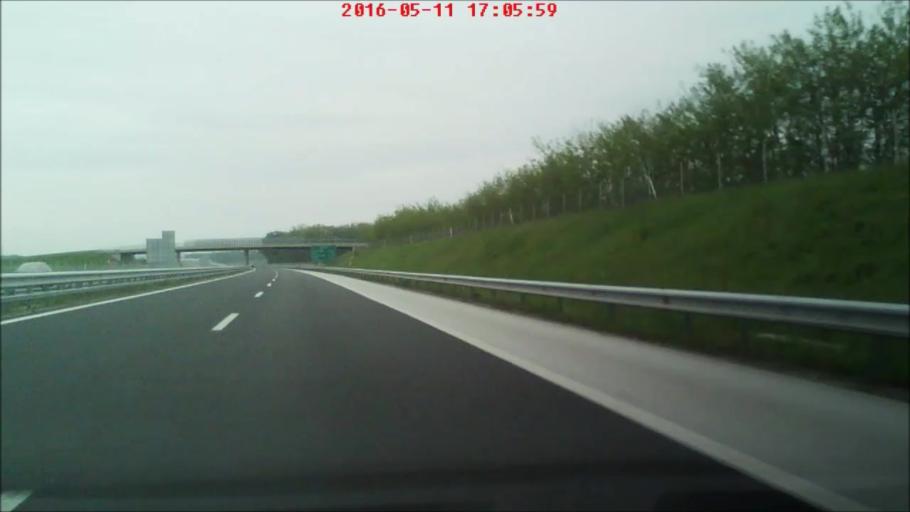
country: SI
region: Kidricevo
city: Kidricevo
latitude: 46.4092
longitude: 15.8153
